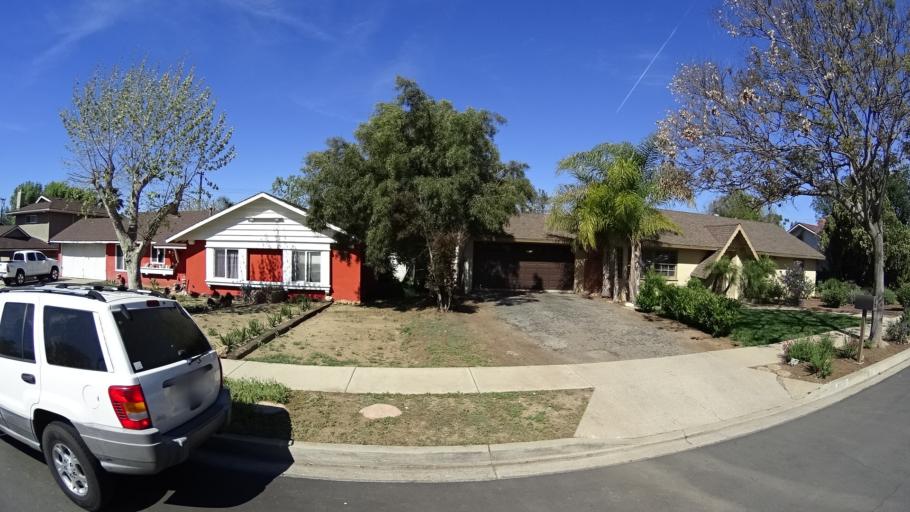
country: US
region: California
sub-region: Ventura County
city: Thousand Oaks
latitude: 34.2212
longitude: -118.8667
